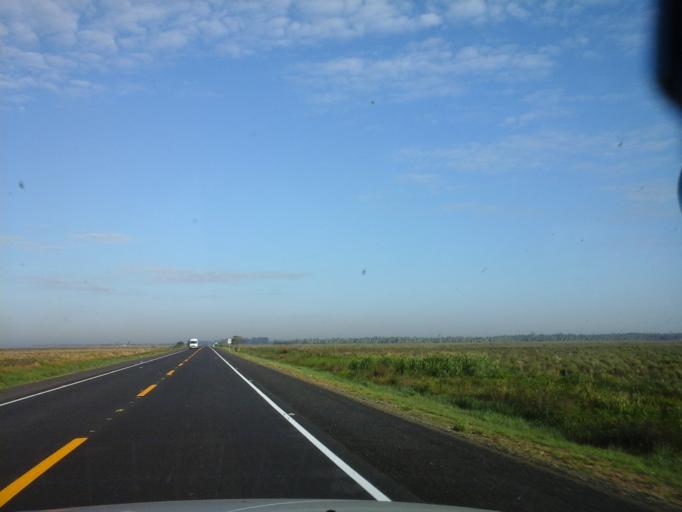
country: PY
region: Neembucu
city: Cerrito
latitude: -26.8682
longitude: -57.7822
